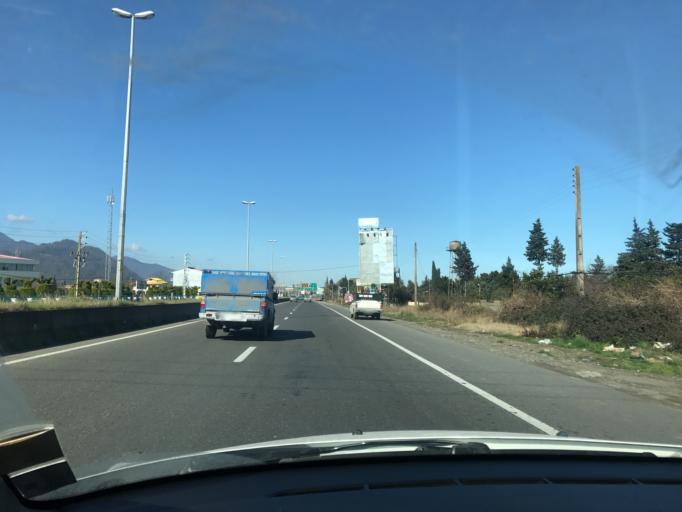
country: IR
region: Mazandaran
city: Ramsar
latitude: 36.9604
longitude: 50.5995
